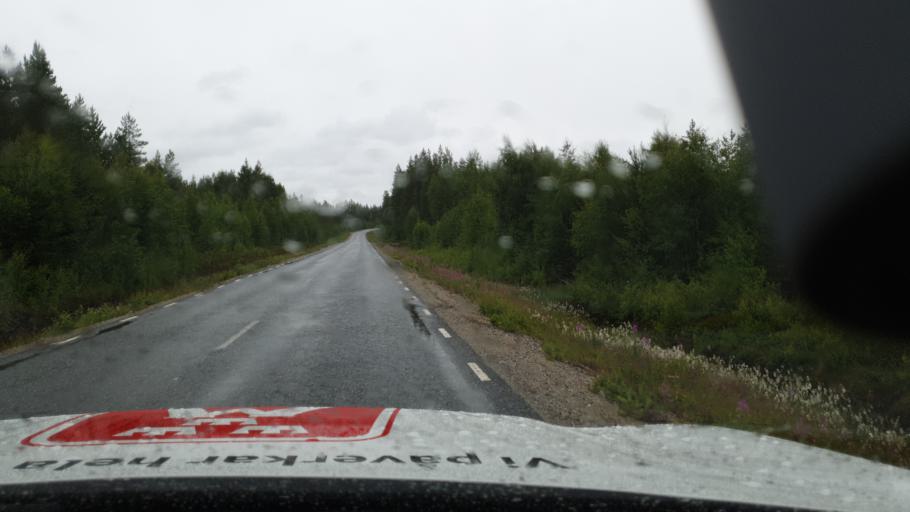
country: SE
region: Vaesterbotten
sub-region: Vindelns Kommun
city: Vindeln
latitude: 64.4265
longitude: 19.7020
